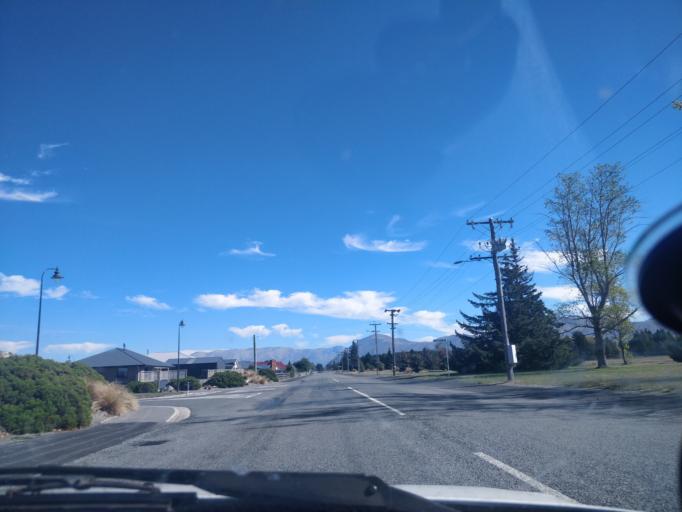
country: NZ
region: Canterbury
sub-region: Timaru District
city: Pleasant Point
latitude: -44.2643
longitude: 170.0963
